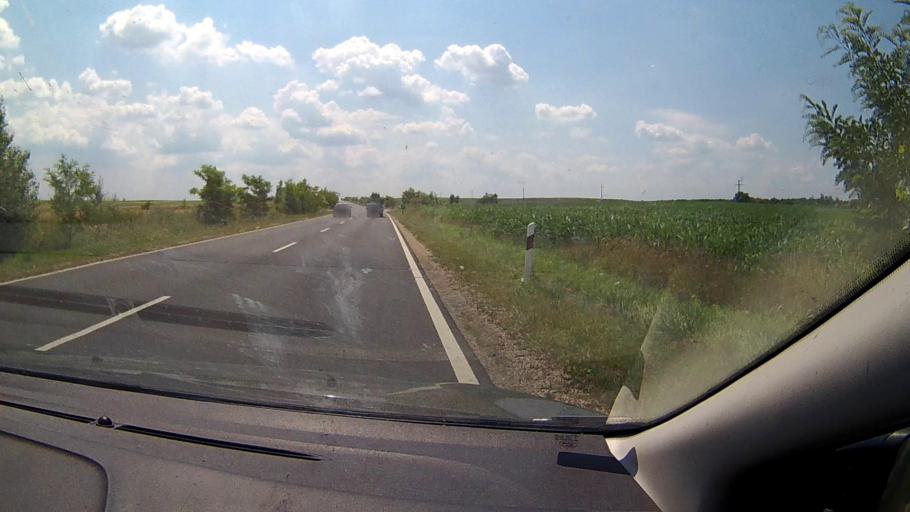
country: HU
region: Komarom-Esztergom
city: Tata
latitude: 47.6029
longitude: 18.3181
